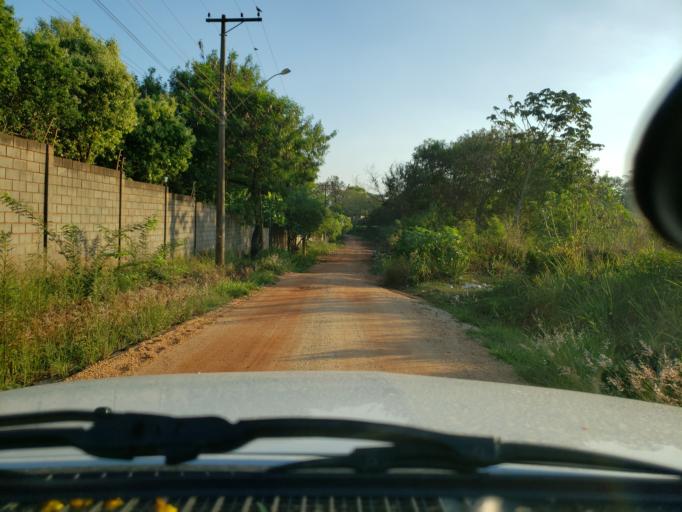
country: BR
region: Sao Paulo
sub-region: Moji-Guacu
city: Mogi-Gaucu
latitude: -22.3379
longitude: -46.9378
